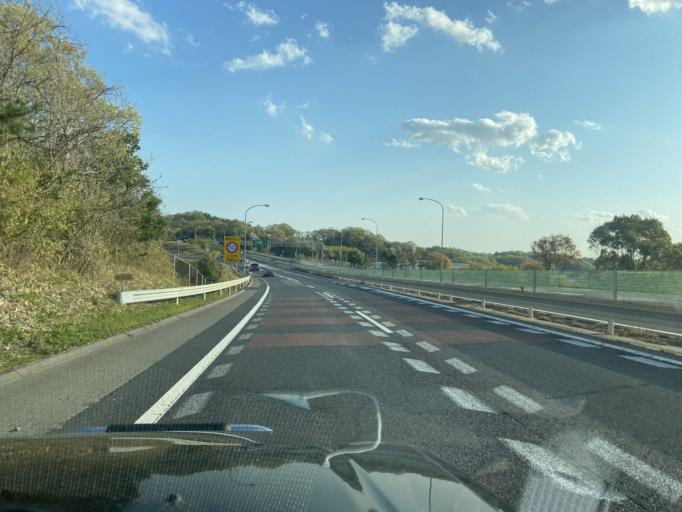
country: JP
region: Hyogo
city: Sandacho
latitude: 34.8968
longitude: 135.1525
